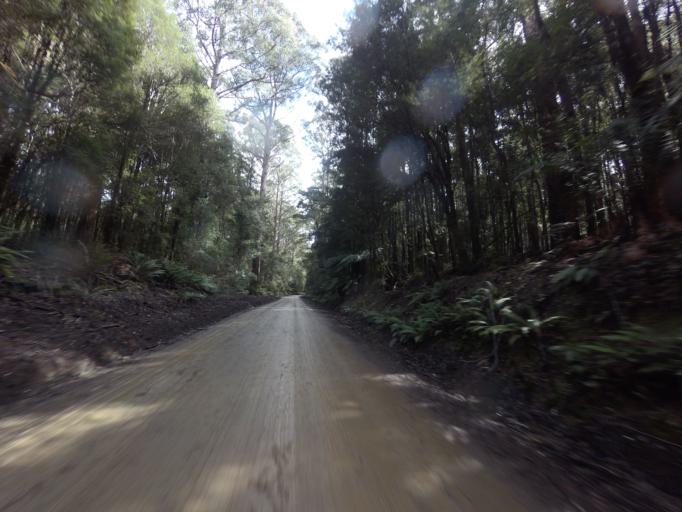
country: AU
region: Tasmania
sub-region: Huon Valley
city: Geeveston
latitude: -43.3850
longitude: 146.8446
